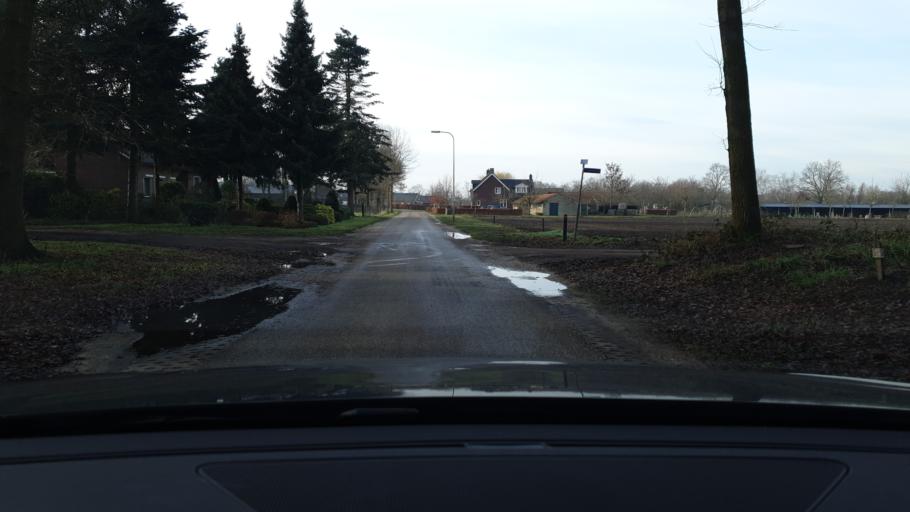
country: NL
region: Limburg
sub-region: Gemeente Peel en Maas
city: Maasbree
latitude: 51.4323
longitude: 6.0577
